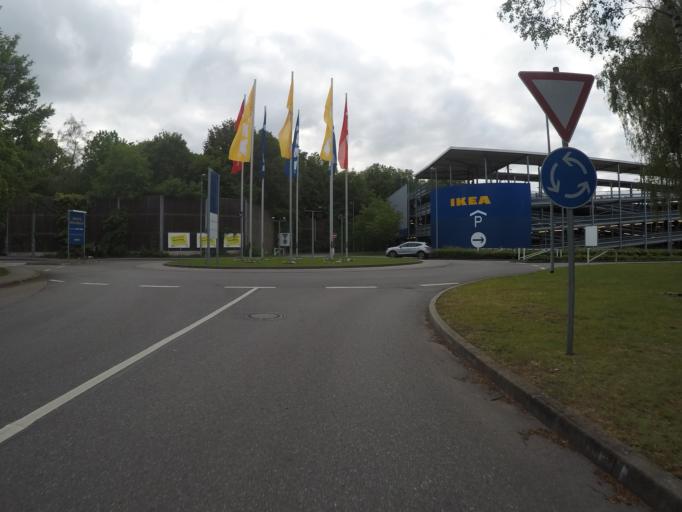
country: DE
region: Schleswig-Holstein
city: Bonningstedt
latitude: 53.6468
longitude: 9.9270
